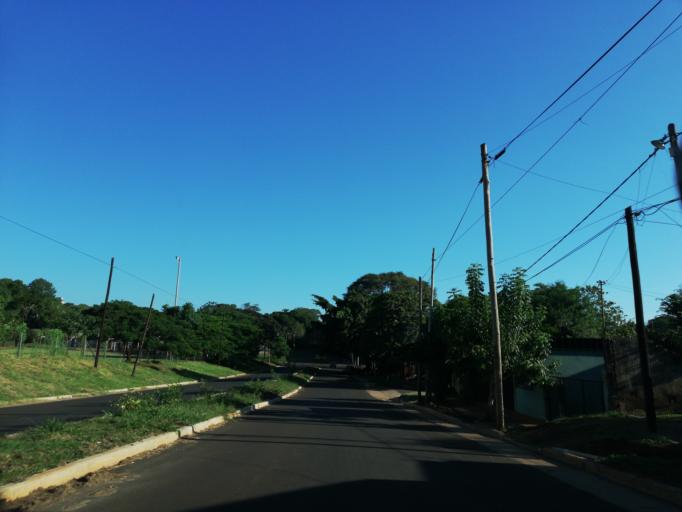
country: AR
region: Misiones
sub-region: Departamento de Capital
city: Posadas
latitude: -27.3635
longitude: -55.9237
